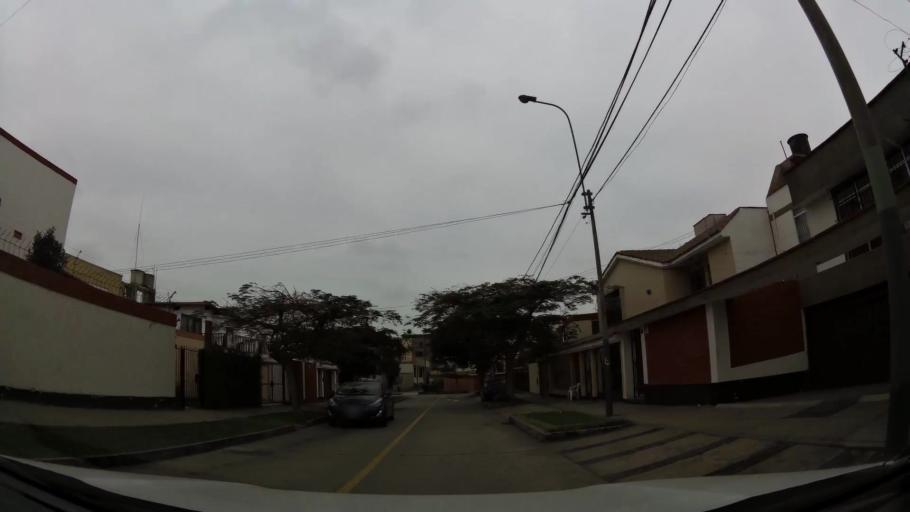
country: PE
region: Lima
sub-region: Lima
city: San Luis
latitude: -12.1048
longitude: -76.9998
